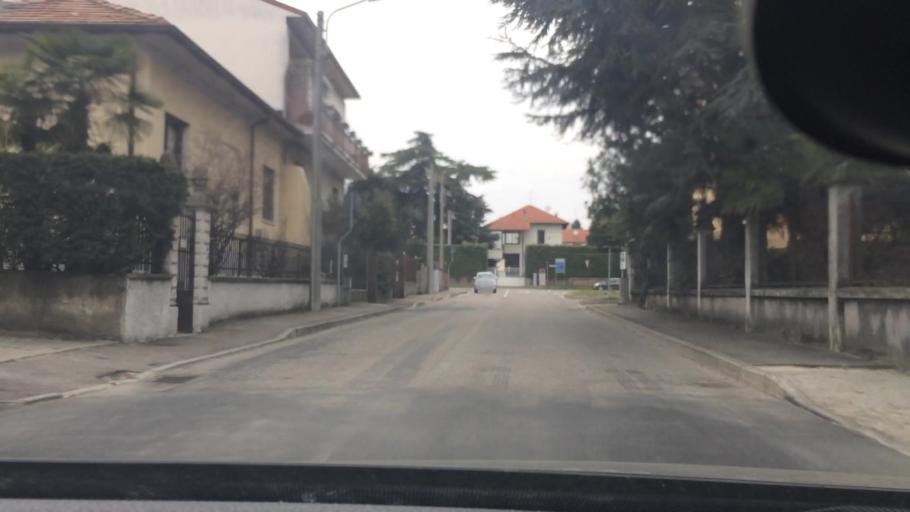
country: IT
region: Lombardy
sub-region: Citta metropolitana di Milano
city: Solaro
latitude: 45.6170
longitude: 9.0767
